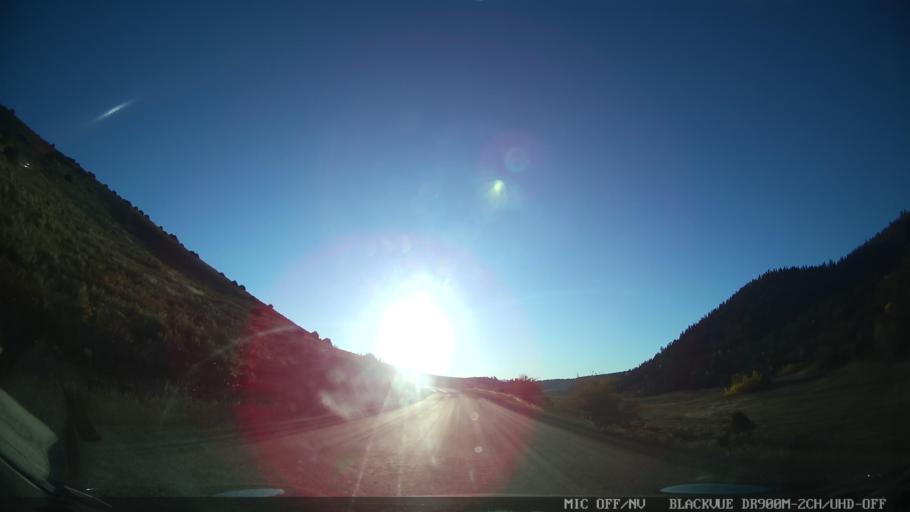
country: US
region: Colorado
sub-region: Grand County
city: Kremmling
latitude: 39.9930
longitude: -106.4548
